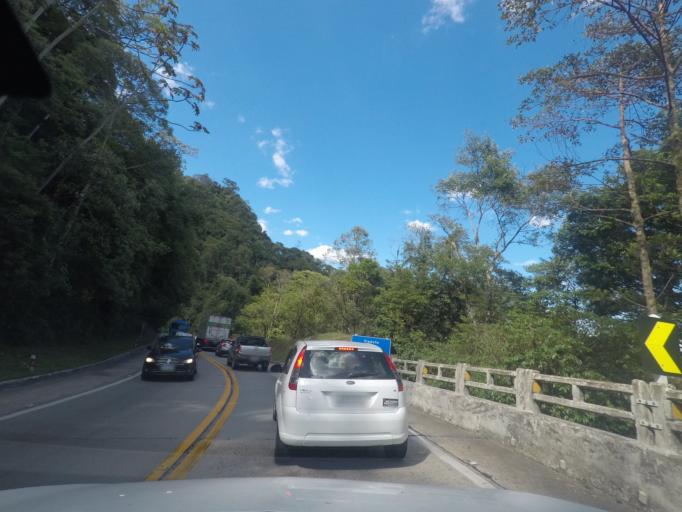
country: BR
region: Rio de Janeiro
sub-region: Guapimirim
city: Guapimirim
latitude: -22.4819
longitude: -42.9985
